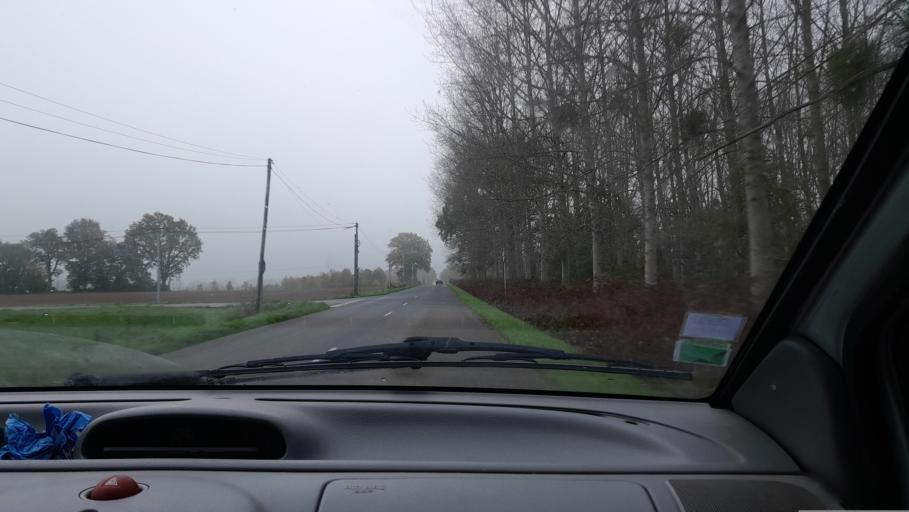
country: FR
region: Brittany
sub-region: Departement d'Ille-et-Vilaine
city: Le Pertre
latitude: 47.9807
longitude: -1.0118
